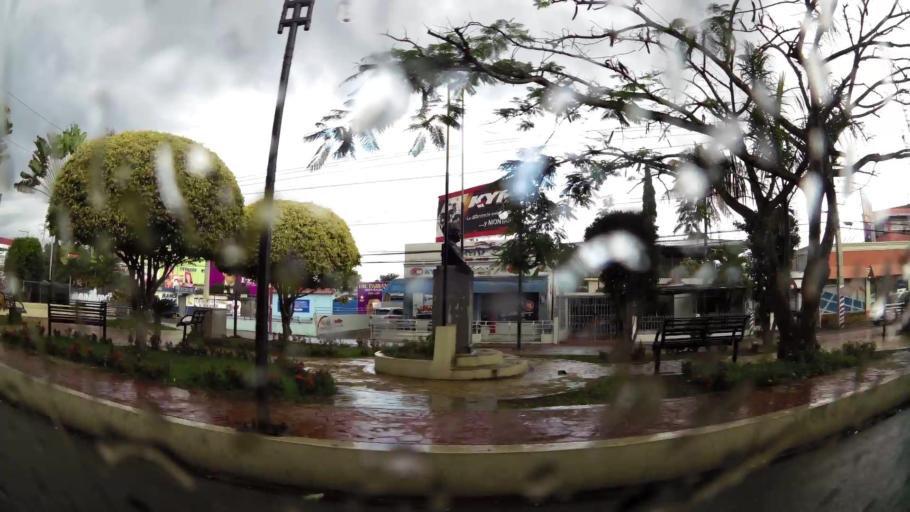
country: DO
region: Monsenor Nouel
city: Bonao
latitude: 18.9367
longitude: -70.4105
